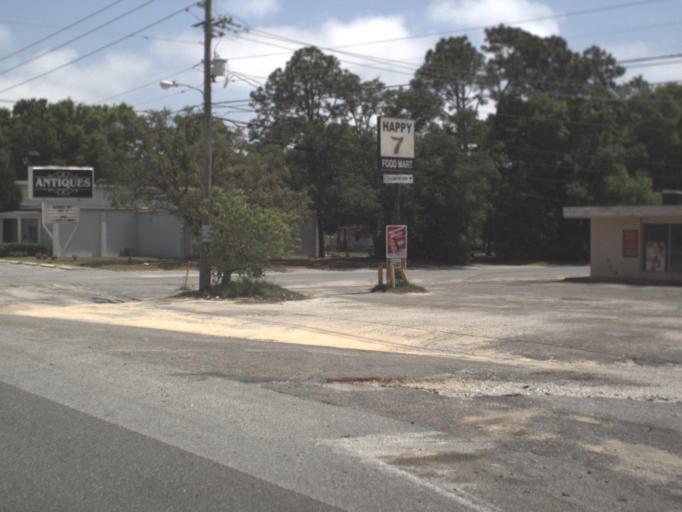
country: US
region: Florida
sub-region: Escambia County
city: West Pensacola
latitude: 30.4100
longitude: -87.2651
